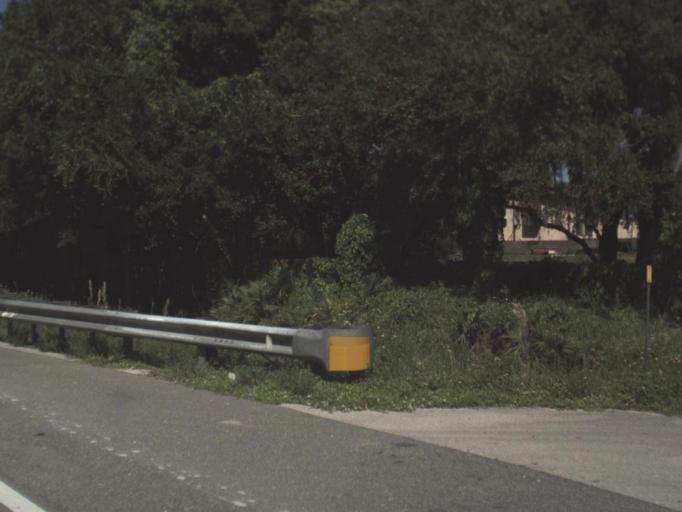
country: US
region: Florida
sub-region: Collier County
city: Lely Resort
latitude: 26.0273
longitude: -81.6428
